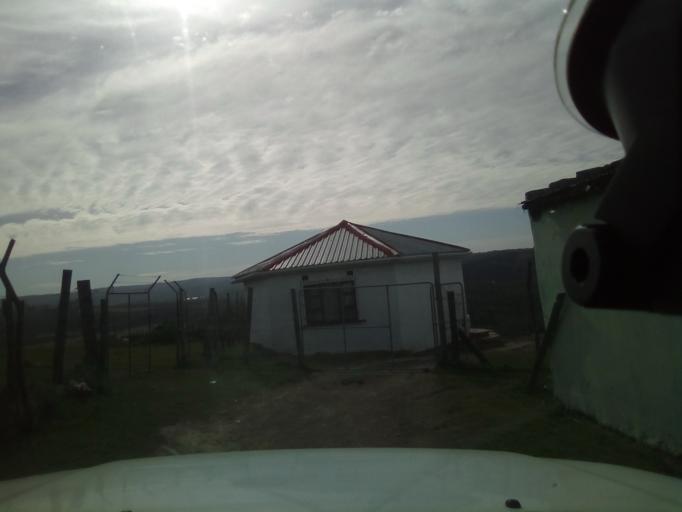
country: ZA
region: Eastern Cape
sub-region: Buffalo City Metropolitan Municipality
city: East London
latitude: -32.7937
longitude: 27.9682
